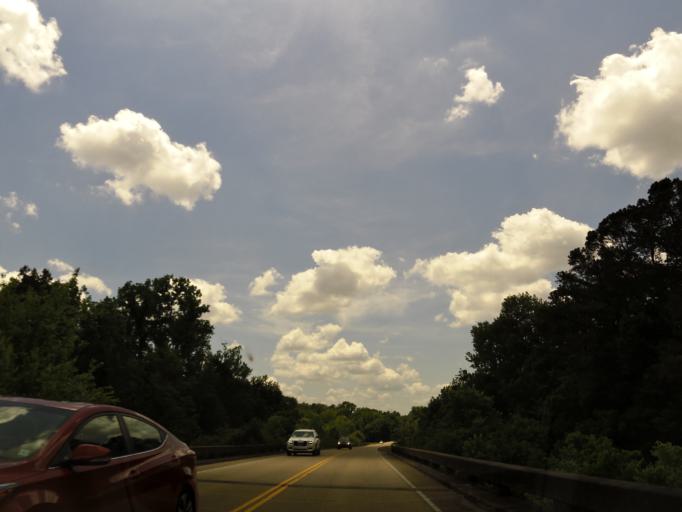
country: US
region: Mississippi
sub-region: Lee County
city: Tupelo
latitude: 34.2793
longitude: -88.7349
